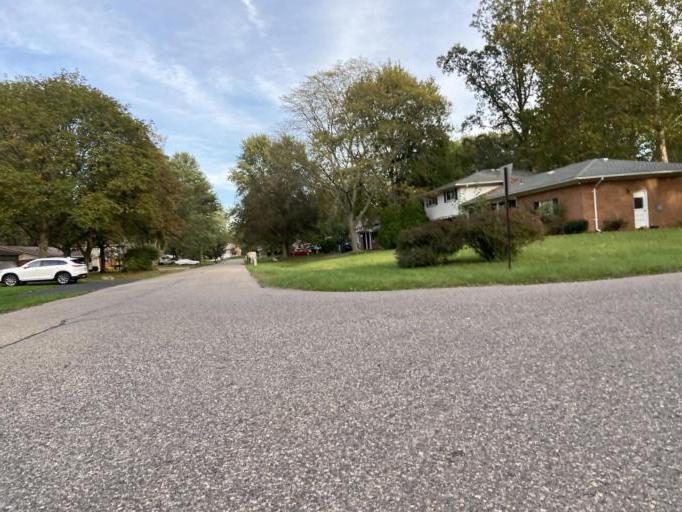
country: US
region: Michigan
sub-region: Oakland County
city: Farmington Hills
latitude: 42.5065
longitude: -83.3719
